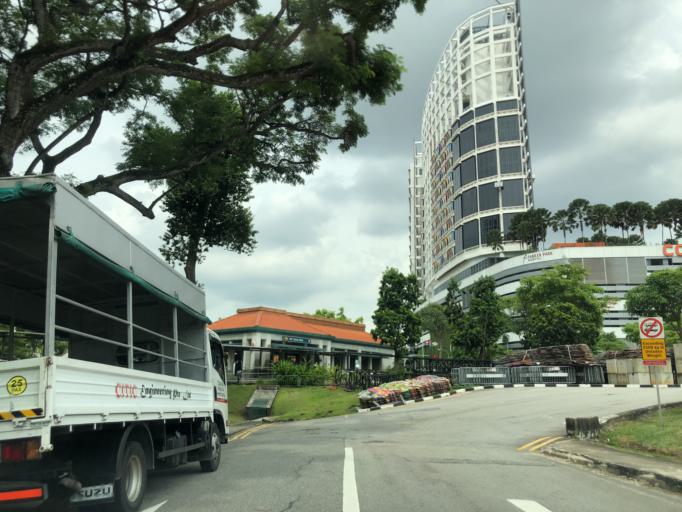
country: SG
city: Singapore
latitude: 1.3114
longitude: 103.8524
